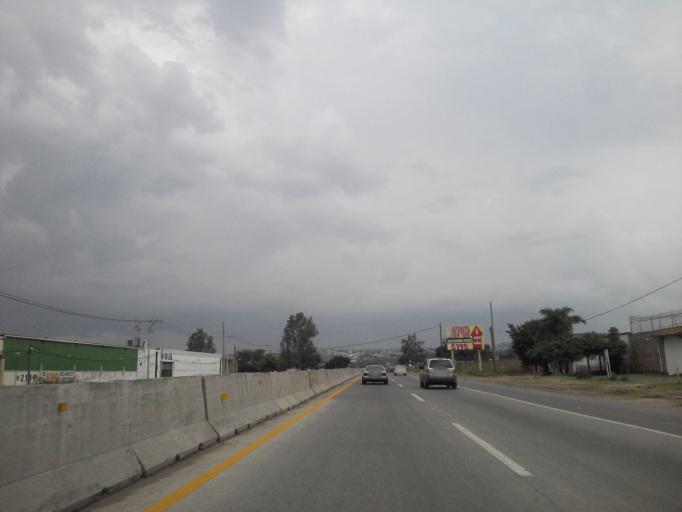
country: MX
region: Jalisco
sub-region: Tonala
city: Colonia Guadalupana
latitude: 20.5906
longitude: -103.2245
